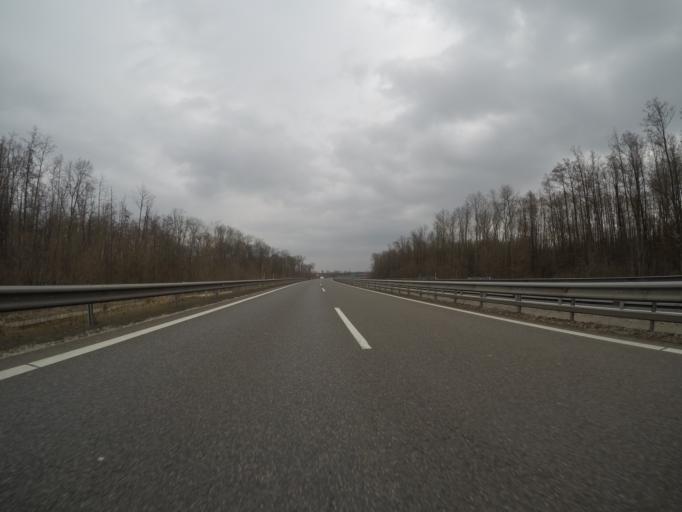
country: SI
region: Velika Polana
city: Velika Polana
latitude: 46.5999
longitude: 16.3994
